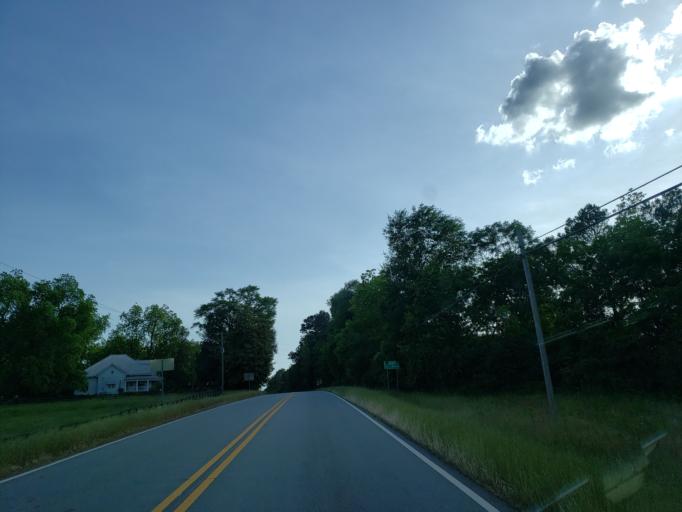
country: US
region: Georgia
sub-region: Carroll County
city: Bowdon
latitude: 33.4713
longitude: -85.2941
